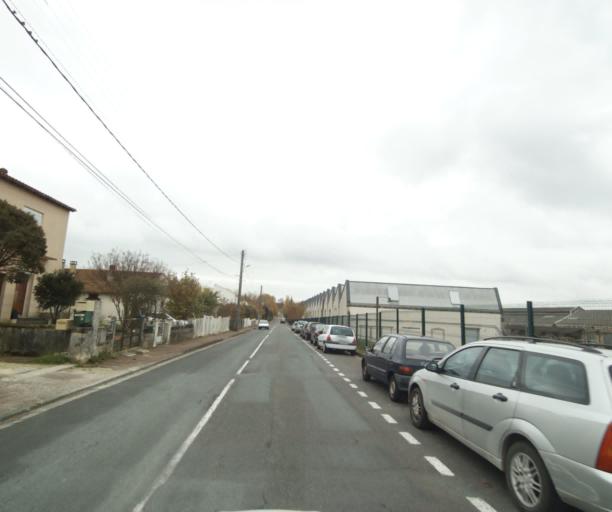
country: FR
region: Poitou-Charentes
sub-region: Departement de la Charente-Maritime
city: Saintes
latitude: 45.7505
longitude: -0.6139
